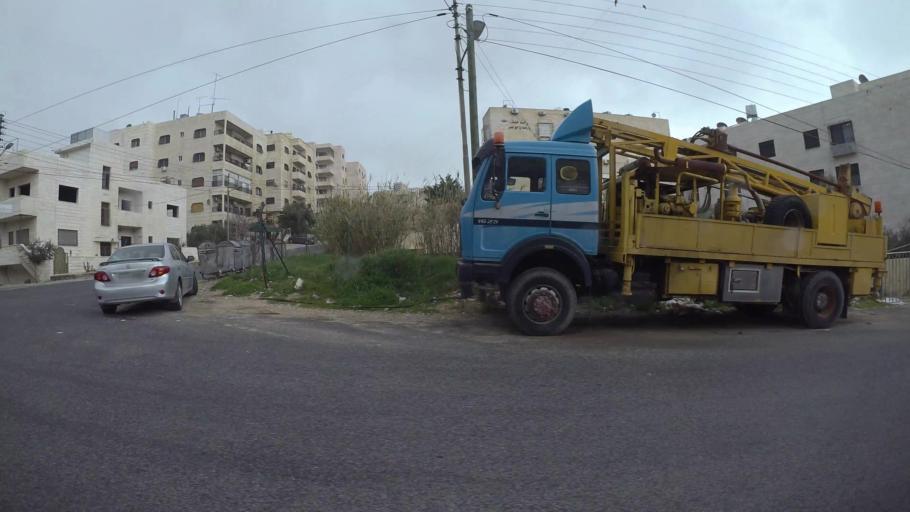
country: JO
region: Amman
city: Al Jubayhah
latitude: 31.9905
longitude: 35.8583
